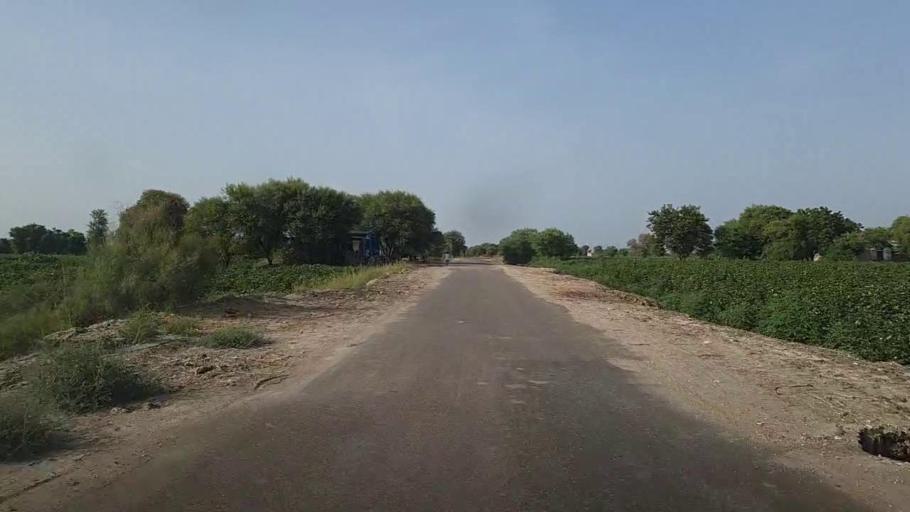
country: PK
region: Sindh
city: Ubauro
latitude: 28.0879
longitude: 69.8435
